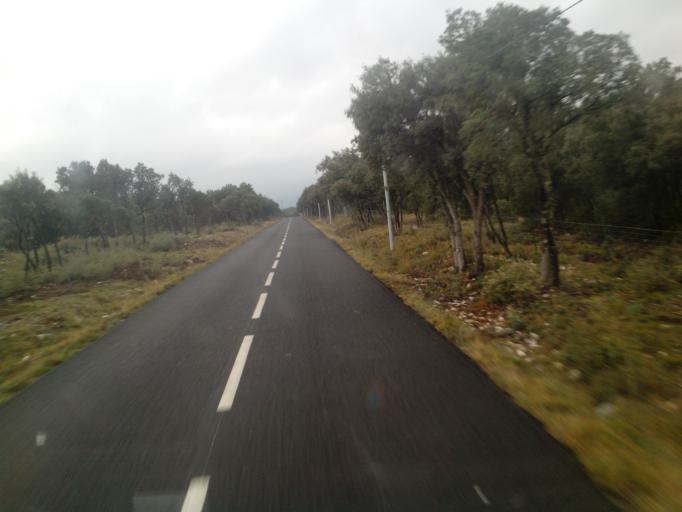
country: FR
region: Languedoc-Roussillon
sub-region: Departement de l'Herault
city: Saint-Jean-de-Fos
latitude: 43.7867
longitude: 3.6124
